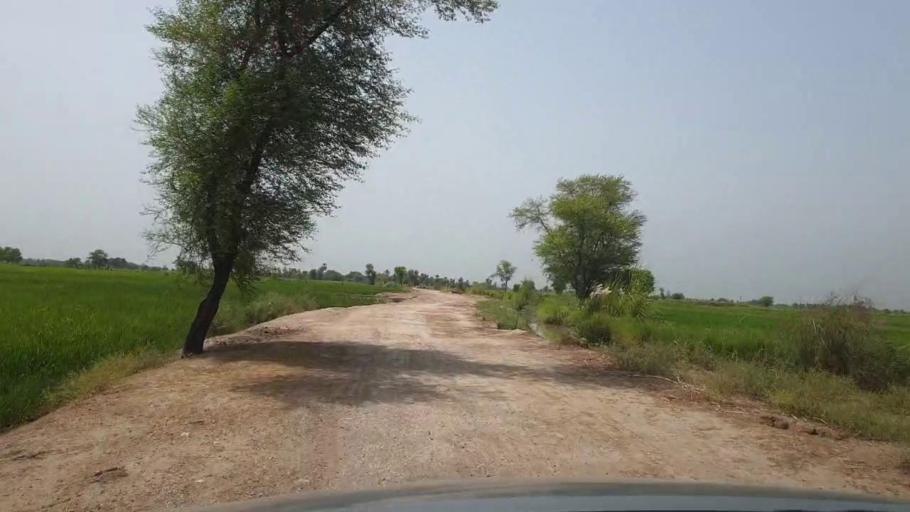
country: PK
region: Sindh
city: Madeji
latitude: 27.7938
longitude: 68.4350
